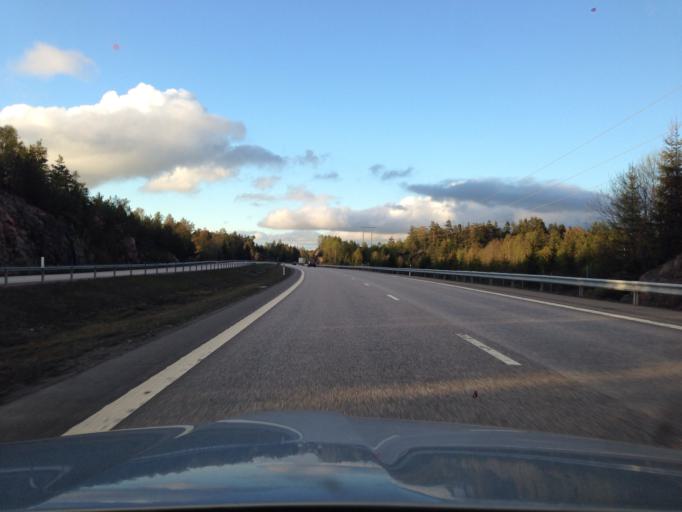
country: SE
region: Soedermanland
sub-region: Oxelosunds Kommun
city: Oxelosund
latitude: 58.8301
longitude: 17.1647
